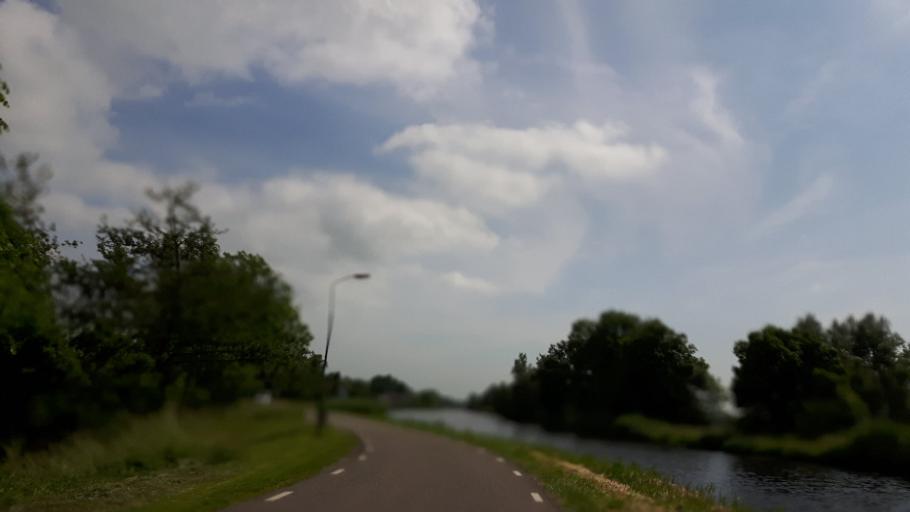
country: NL
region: Utrecht
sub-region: Gemeente De Ronde Venen
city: Mijdrecht
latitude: 52.1674
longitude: 4.8685
